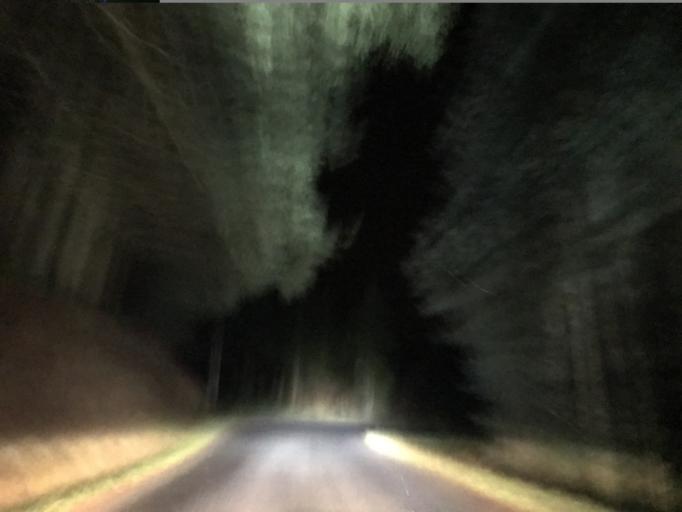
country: FR
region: Auvergne
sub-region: Departement du Puy-de-Dome
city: Saint-Remy-sur-Durolle
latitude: 45.9141
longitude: 3.6316
